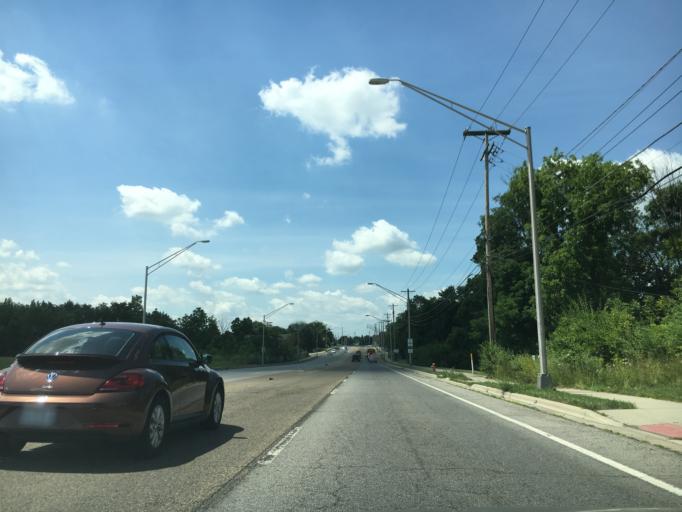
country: US
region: Ohio
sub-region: Franklin County
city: Lincoln Village
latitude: 39.9386
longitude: -83.1435
